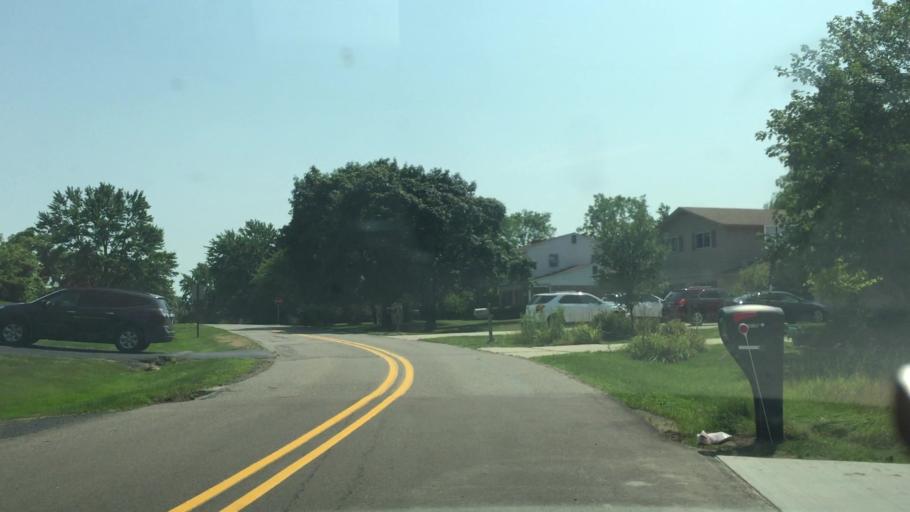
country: US
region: Michigan
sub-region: Oakland County
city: West Bloomfield Township
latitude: 42.5337
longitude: -83.3548
